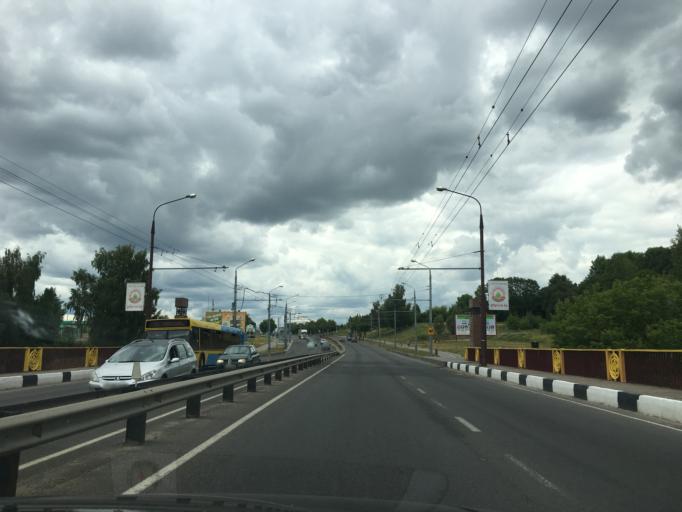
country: BY
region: Grodnenskaya
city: Hrodna
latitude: 53.6620
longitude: 23.8600
